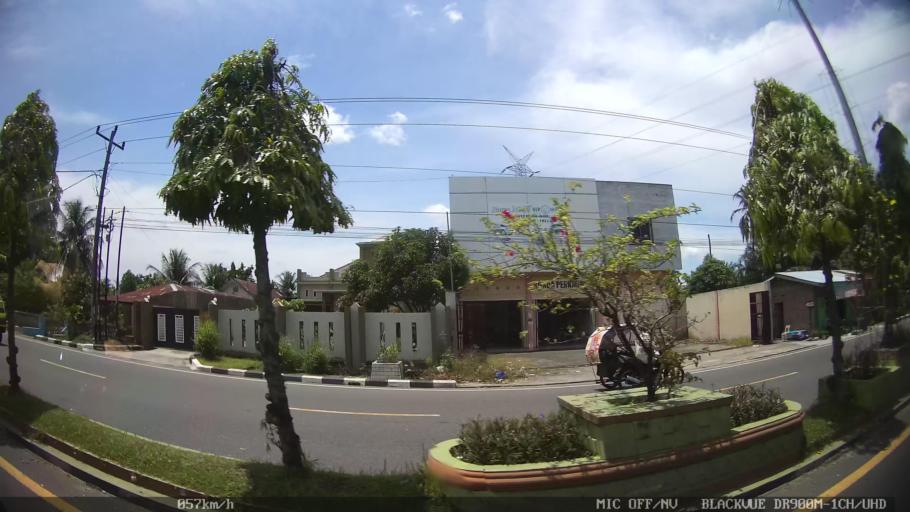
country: ID
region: North Sumatra
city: Binjai
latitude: 3.6087
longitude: 98.5082
